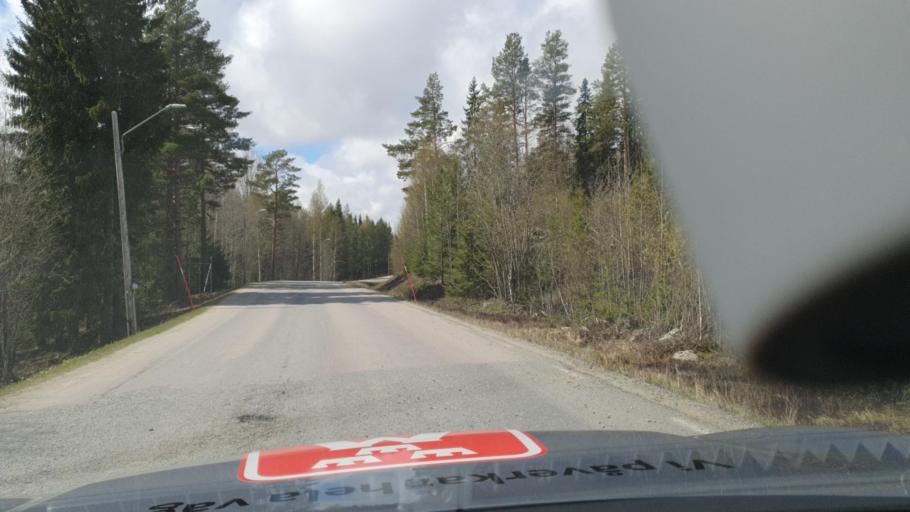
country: SE
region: Vaesternorrland
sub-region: OErnskoeldsviks Kommun
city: Ornskoldsvik
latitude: 63.6929
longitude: 18.8551
